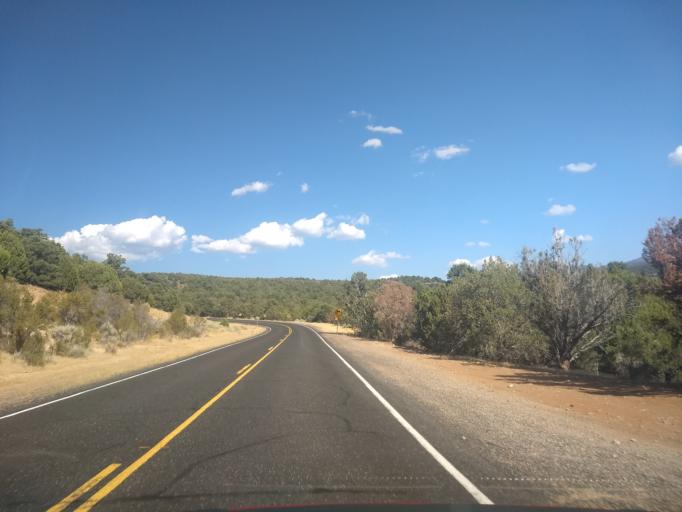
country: US
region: Utah
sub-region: Washington County
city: Enterprise
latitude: 37.4166
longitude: -113.6019
